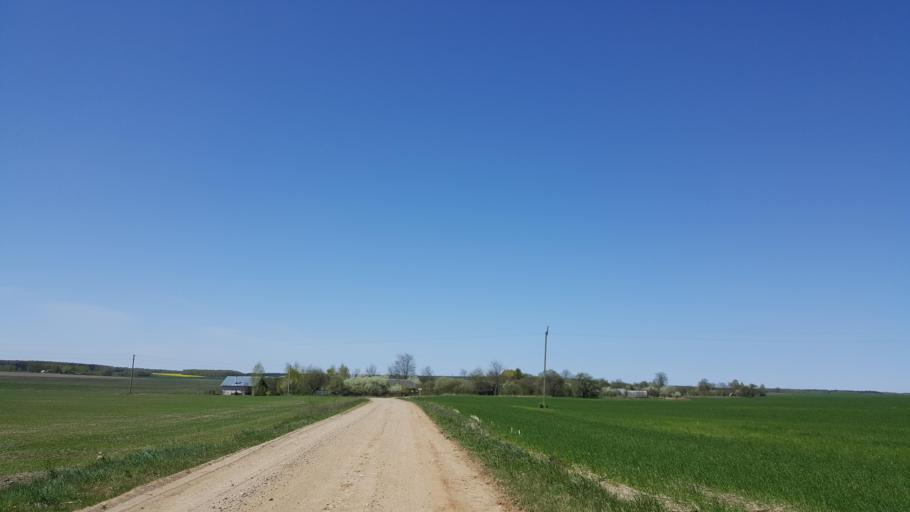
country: BY
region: Brest
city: Charnawchytsy
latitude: 52.3167
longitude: 23.7348
